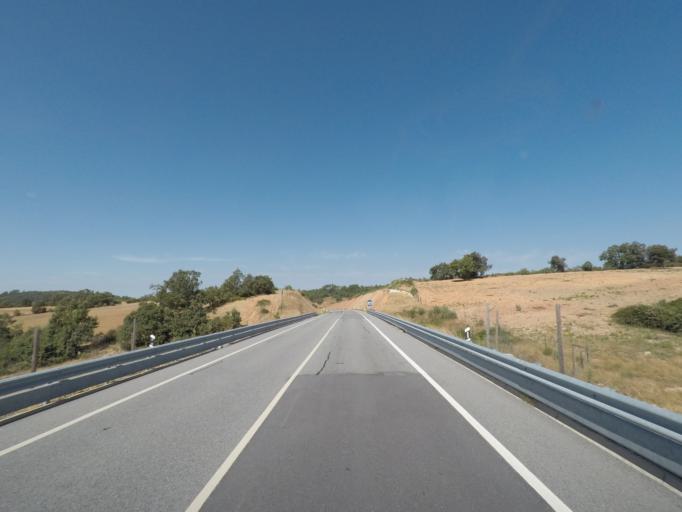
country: PT
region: Braganca
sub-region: Mogadouro
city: Mogadouro
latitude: 41.3469
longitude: -6.6357
